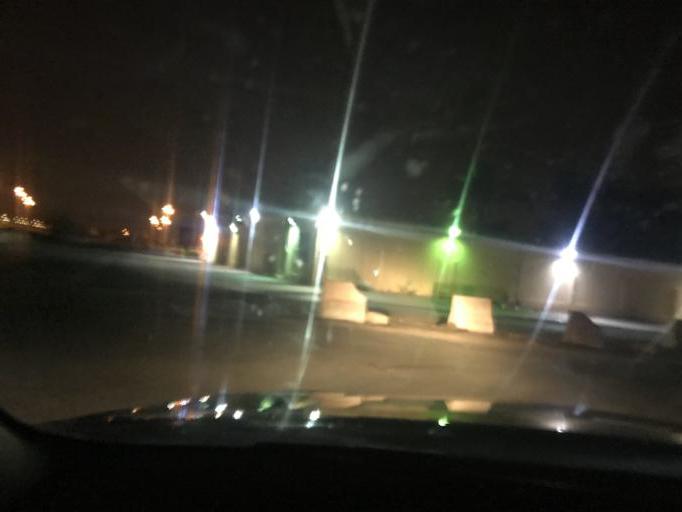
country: SA
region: Ar Riyad
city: Riyadh
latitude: 24.8110
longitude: 46.7180
